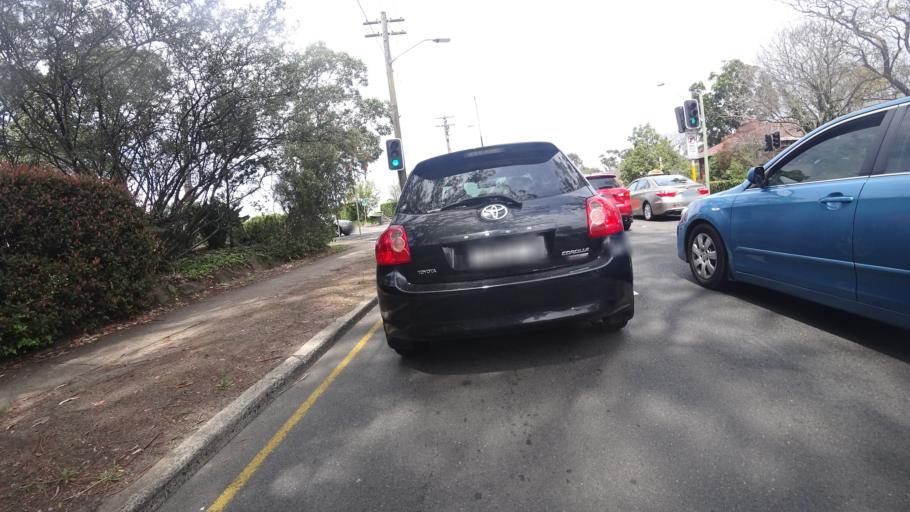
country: AU
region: New South Wales
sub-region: Ku-ring-gai
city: Killara
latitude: -33.7649
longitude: 151.1569
